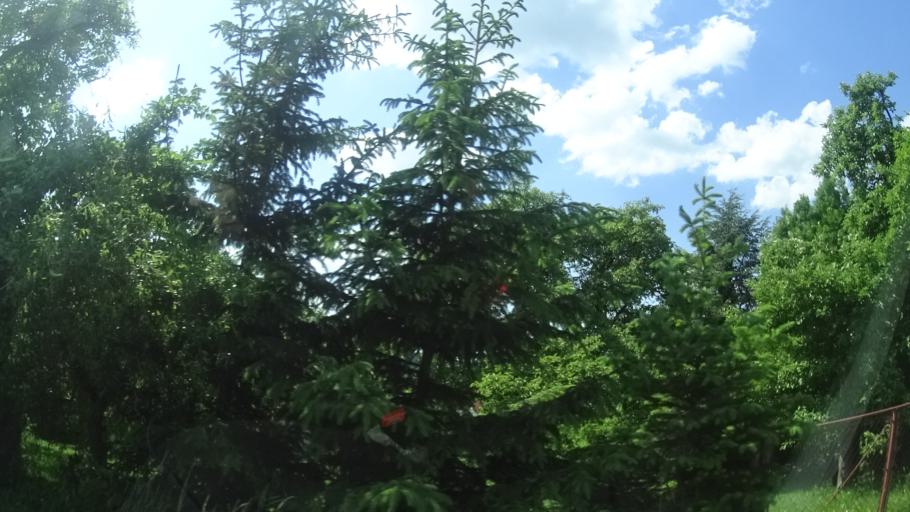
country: DE
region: Hesse
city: Tann
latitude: 50.6407
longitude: 10.0301
